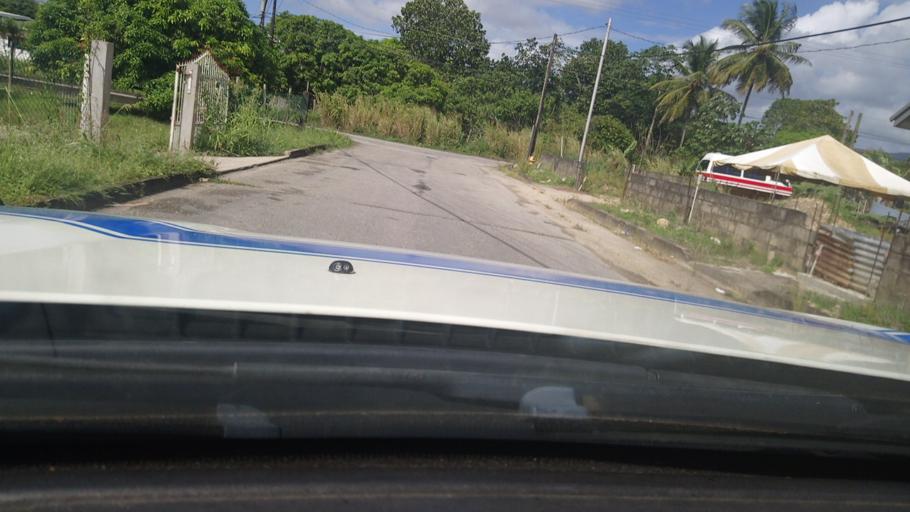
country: TT
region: Borough of Arima
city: Arima
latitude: 10.6181
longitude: -61.2996
